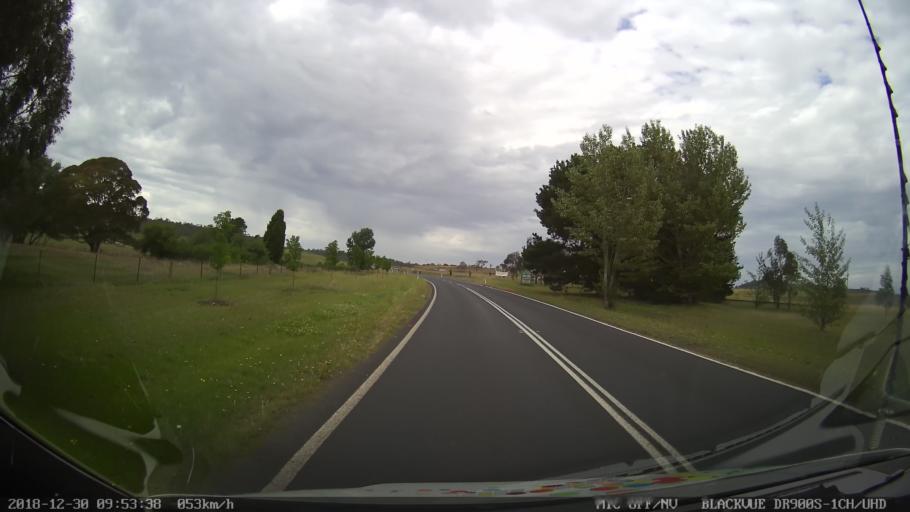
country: AU
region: New South Wales
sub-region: Cooma-Monaro
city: Cooma
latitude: -36.5171
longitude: 149.2814
